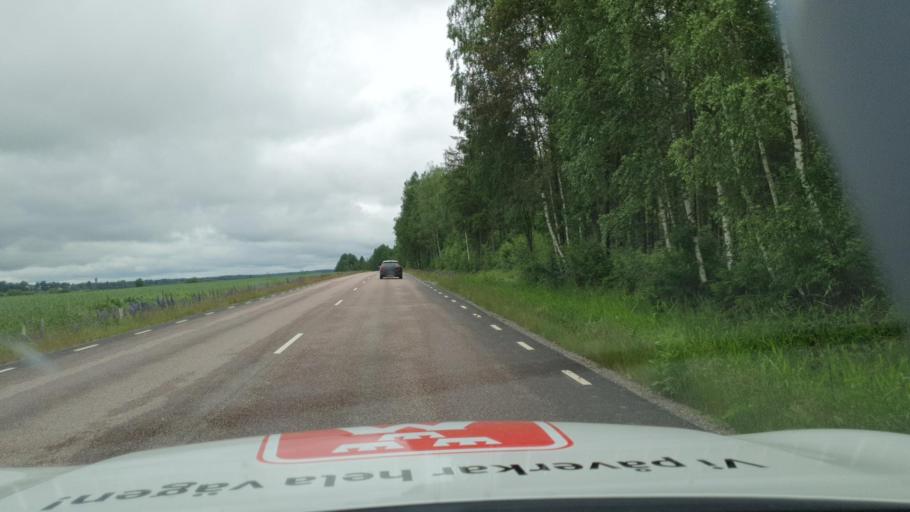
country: SE
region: Vaermland
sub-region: Karlstads Kommun
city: Edsvalla
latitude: 59.4108
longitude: 13.2129
